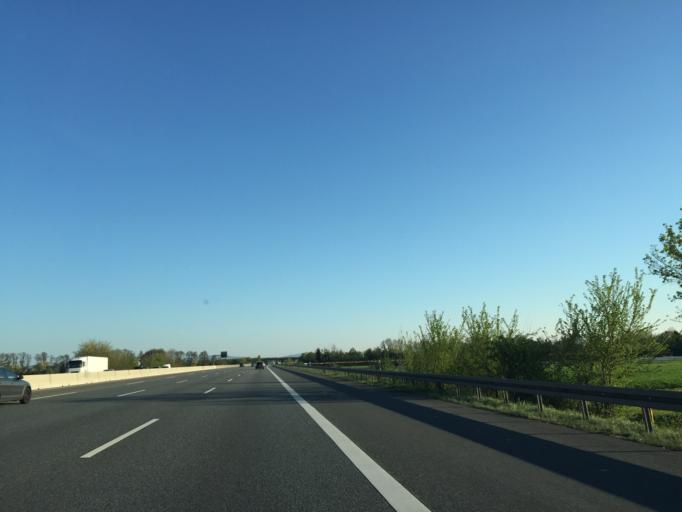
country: DE
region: Hesse
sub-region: Regierungsbezirk Darmstadt
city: Erzhausen
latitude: 49.9383
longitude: 8.6118
